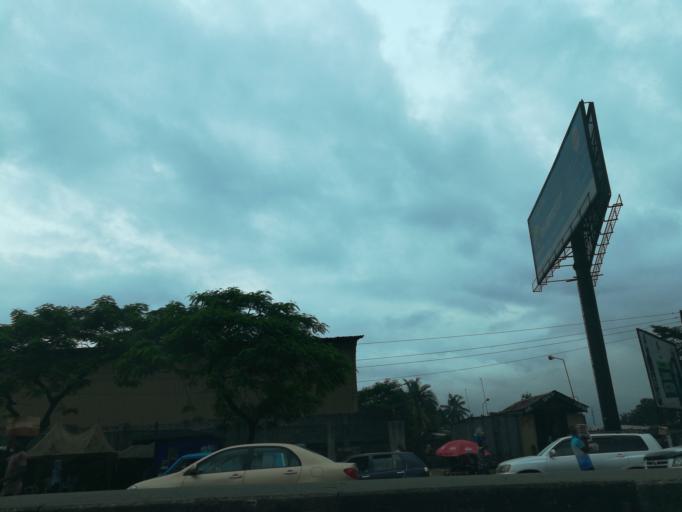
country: NG
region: Rivers
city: Port Harcourt
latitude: 4.8439
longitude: 7.0389
